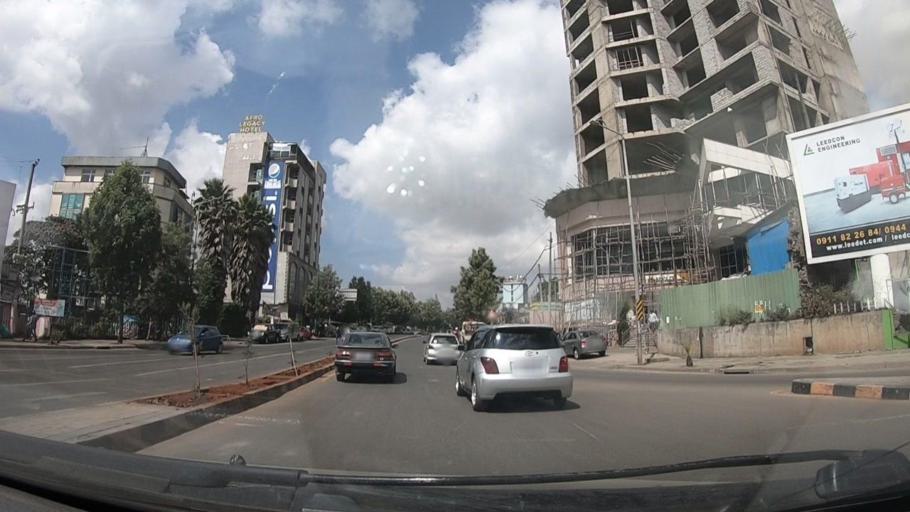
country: ET
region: Adis Abeba
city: Addis Ababa
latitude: 9.0002
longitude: 38.7397
